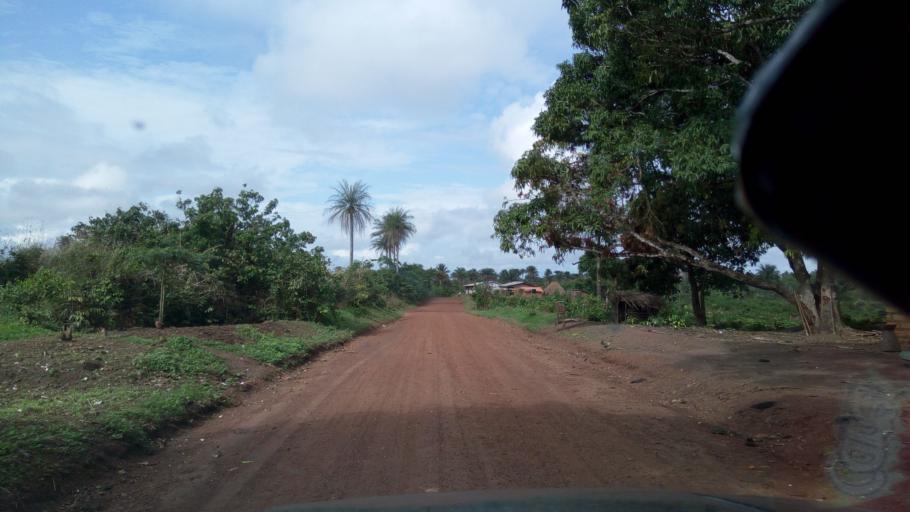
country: SL
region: Northern Province
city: Pepel
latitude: 8.6535
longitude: -13.0076
